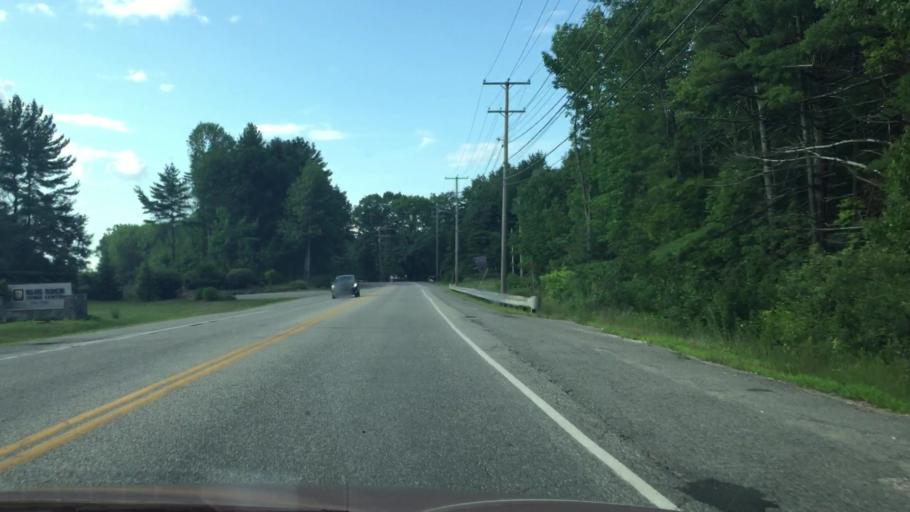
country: US
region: Maine
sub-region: Cumberland County
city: Westbrook
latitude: 43.6538
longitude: -70.3597
